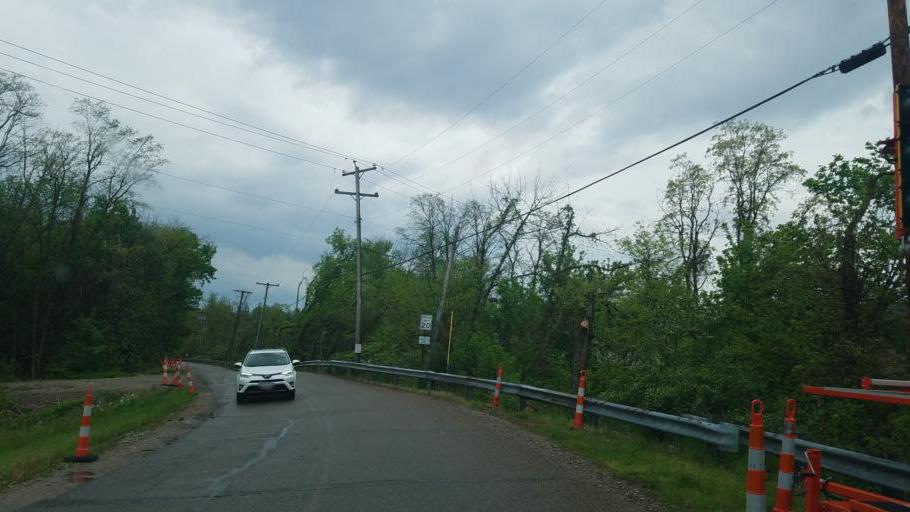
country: US
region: Ohio
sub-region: Fairfield County
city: Millersport
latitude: 39.9069
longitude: -82.5330
